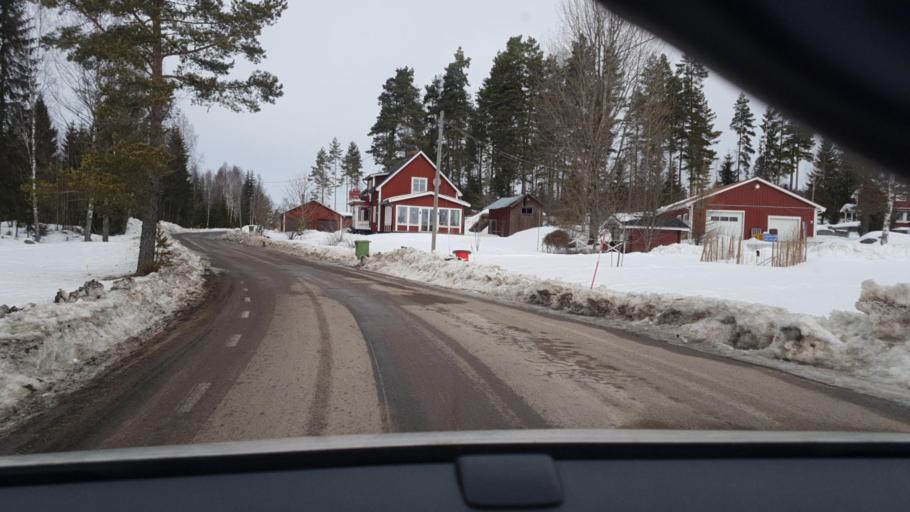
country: SE
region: Vaermland
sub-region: Eda Kommun
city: Charlottenberg
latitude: 59.8621
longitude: 12.3453
